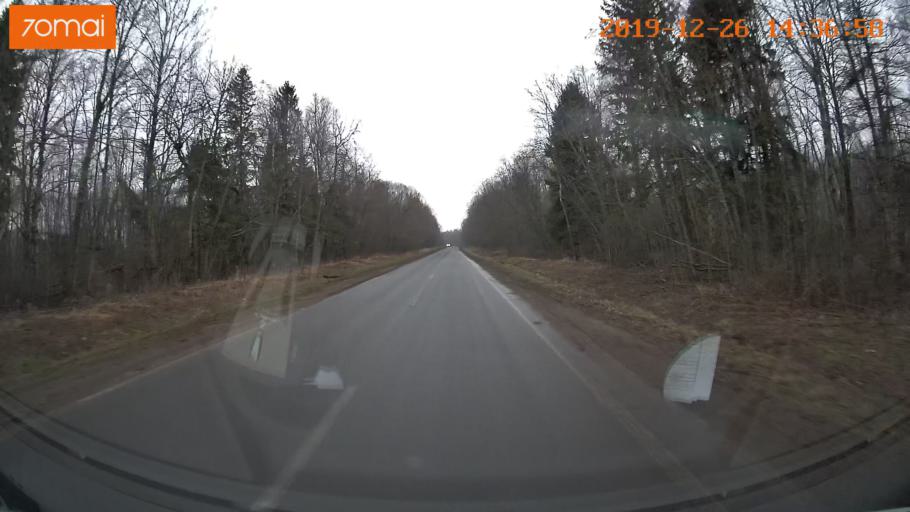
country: RU
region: Jaroslavl
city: Poshekhon'ye
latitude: 58.4066
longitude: 38.9741
